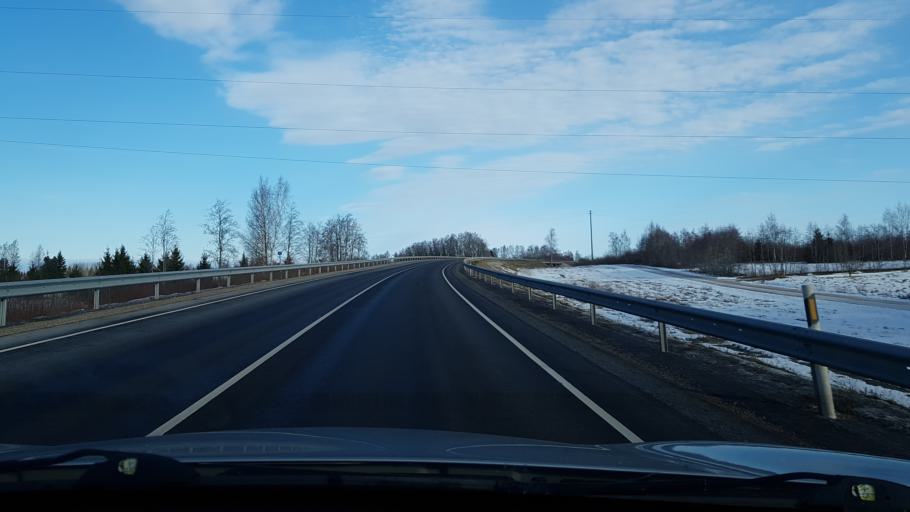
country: EE
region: Viljandimaa
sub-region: Viljandi linn
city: Viljandi
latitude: 58.3860
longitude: 25.5607
